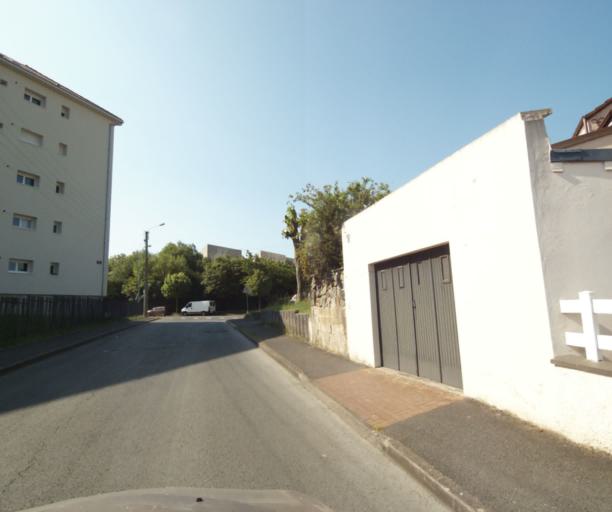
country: FR
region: Champagne-Ardenne
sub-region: Departement des Ardennes
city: Charleville-Mezieres
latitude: 49.7780
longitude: 4.7031
